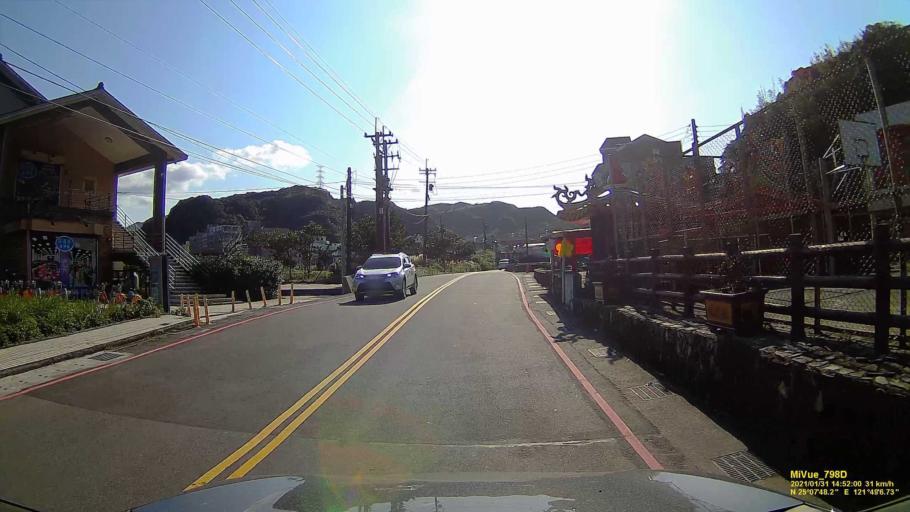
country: TW
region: Taiwan
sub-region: Keelung
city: Keelung
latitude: 25.1298
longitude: 121.8183
